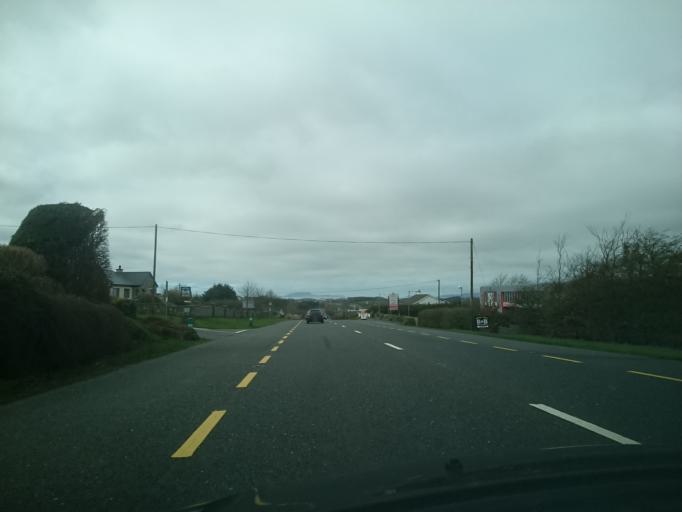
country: IE
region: Connaught
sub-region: Maigh Eo
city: Westport
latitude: 53.8034
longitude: -9.4892
